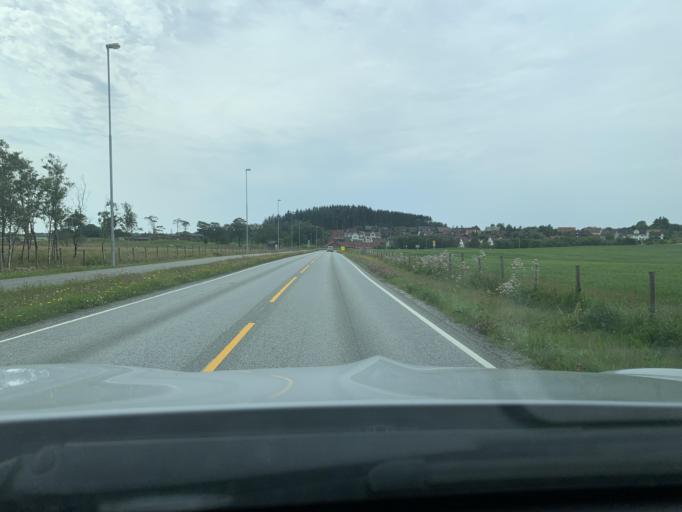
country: NO
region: Rogaland
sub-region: Time
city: Bryne
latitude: 58.7344
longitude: 5.6825
